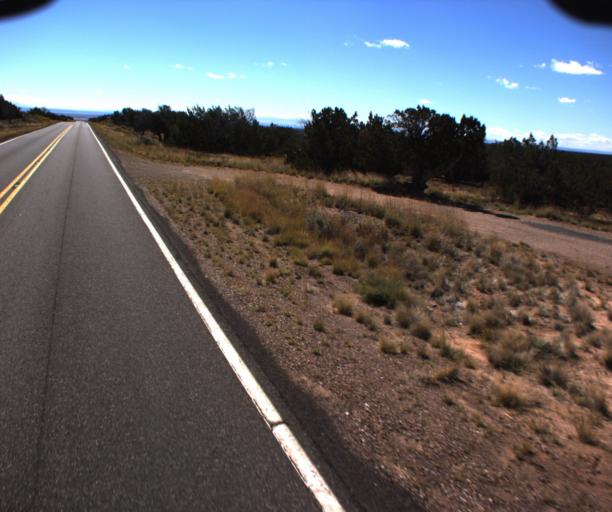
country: US
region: Arizona
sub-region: Apache County
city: Saint Johns
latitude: 34.8418
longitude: -109.2376
